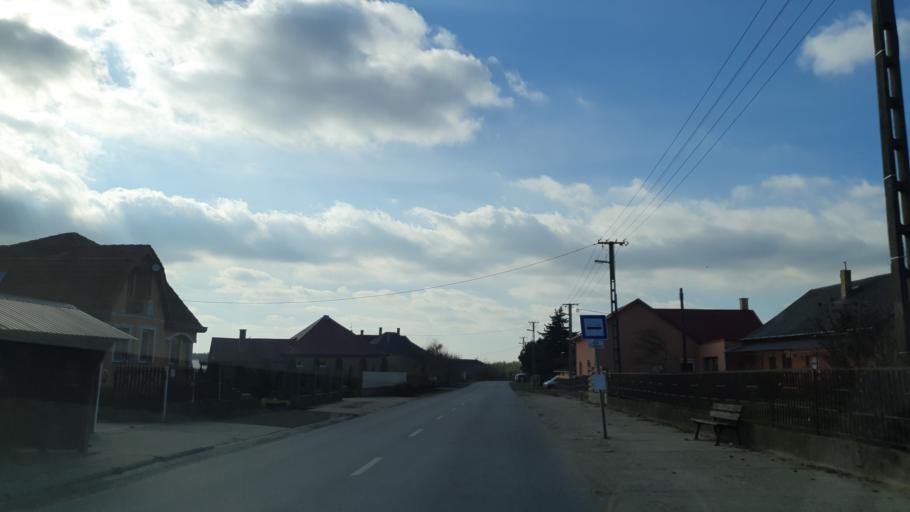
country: HU
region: Szabolcs-Szatmar-Bereg
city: Nyirkarasz
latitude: 48.0944
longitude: 22.0977
